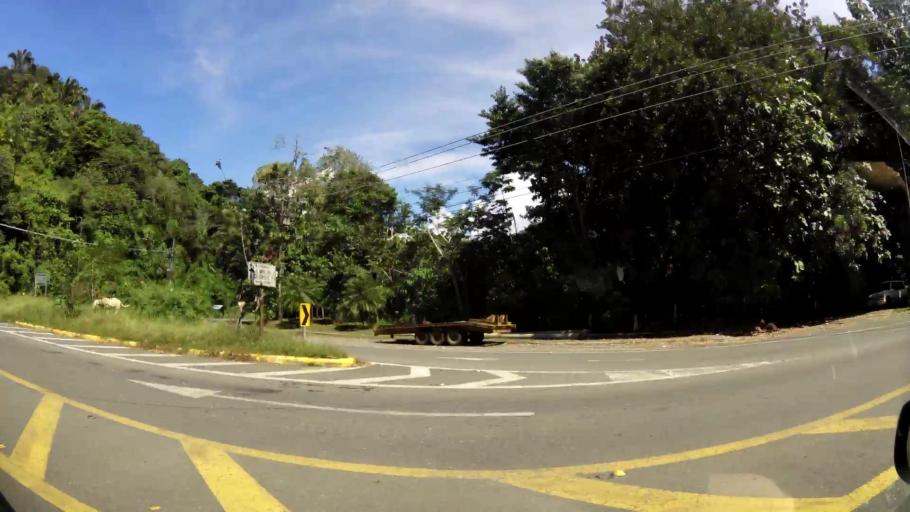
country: CR
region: San Jose
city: San Isidro
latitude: 9.2589
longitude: -83.8641
